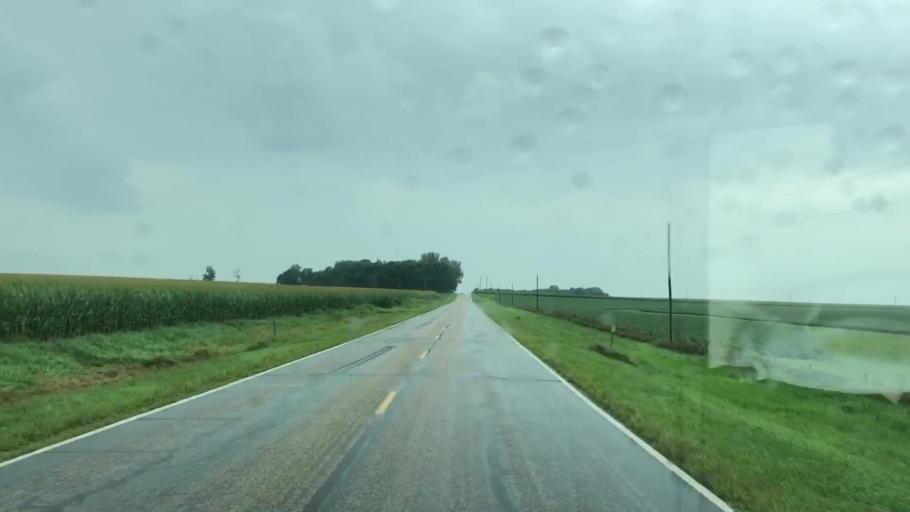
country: US
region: Iowa
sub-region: O'Brien County
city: Sanborn
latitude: 43.2728
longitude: -95.7171
